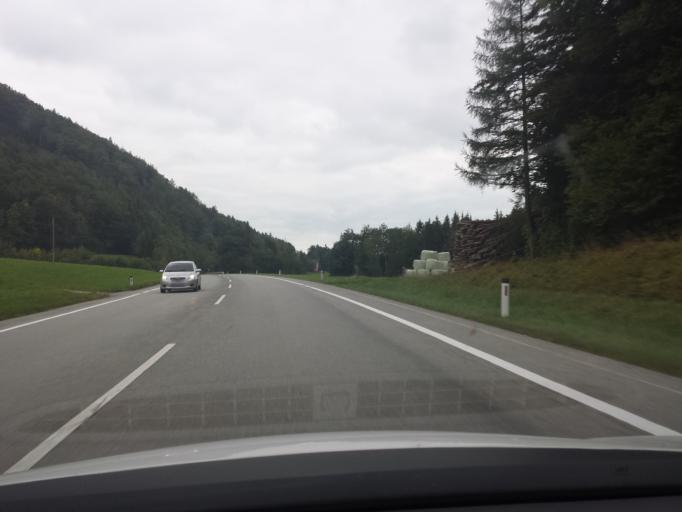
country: AT
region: Salzburg
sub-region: Politischer Bezirk Salzburg-Umgebung
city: Fuschl am See
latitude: 47.7955
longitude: 13.2803
